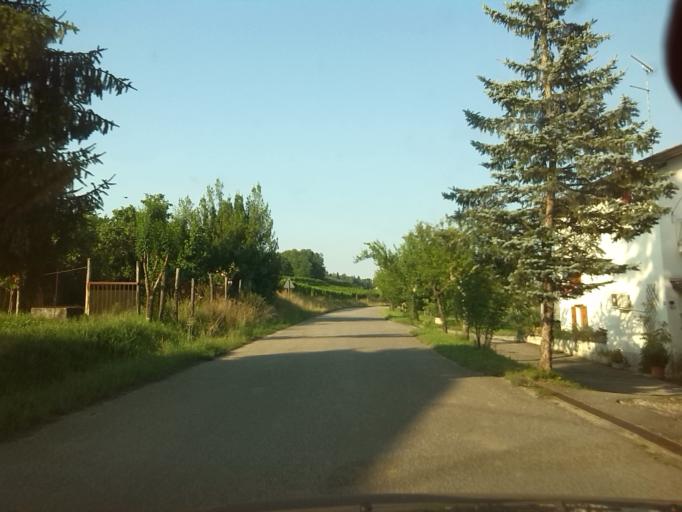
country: IT
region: Friuli Venezia Giulia
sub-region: Provincia di Gorizia
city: Cormons
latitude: 45.9820
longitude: 13.4729
